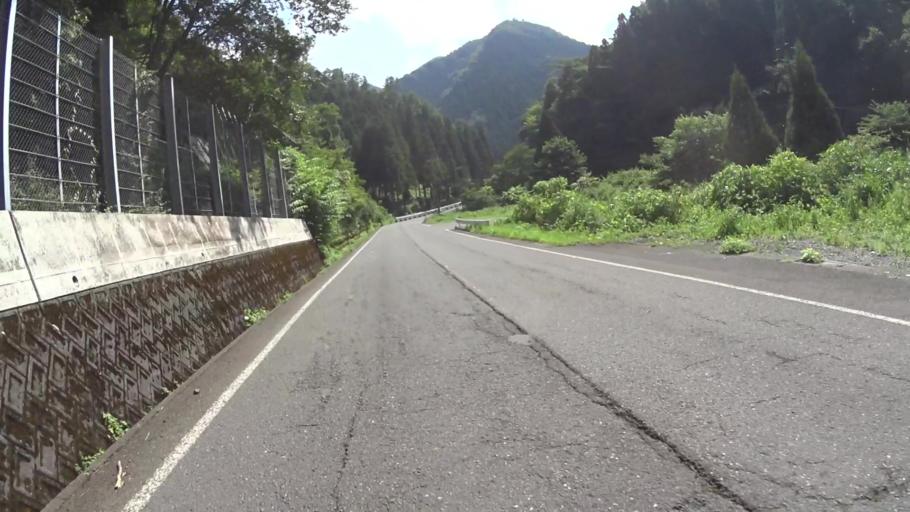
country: JP
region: Fukui
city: Obama
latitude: 35.3907
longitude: 135.5841
